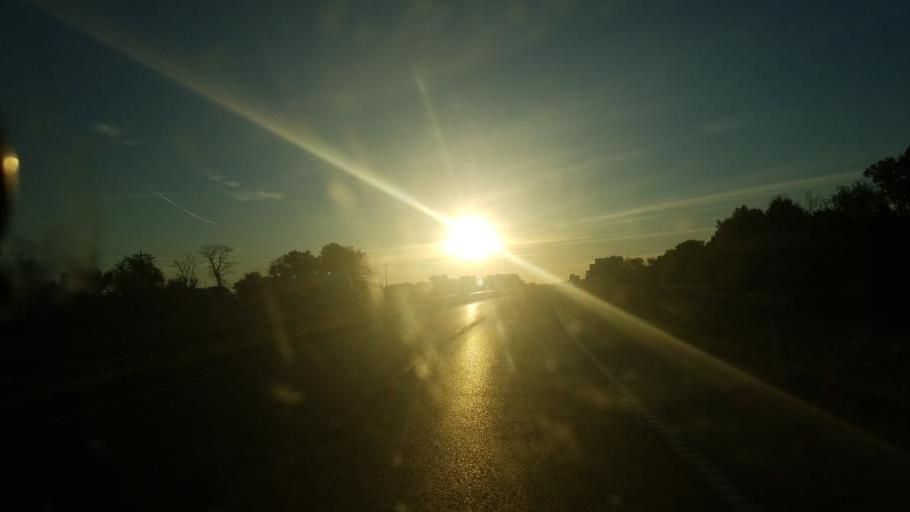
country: US
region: Missouri
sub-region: Callaway County
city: Fulton
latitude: 38.9513
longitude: -91.9657
